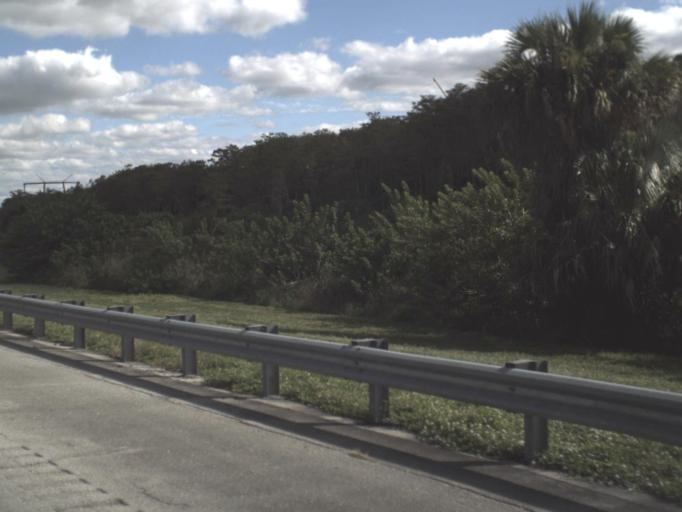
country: US
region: Florida
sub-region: Indian River County
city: West Vero Corridor
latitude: 27.5586
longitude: -80.6470
